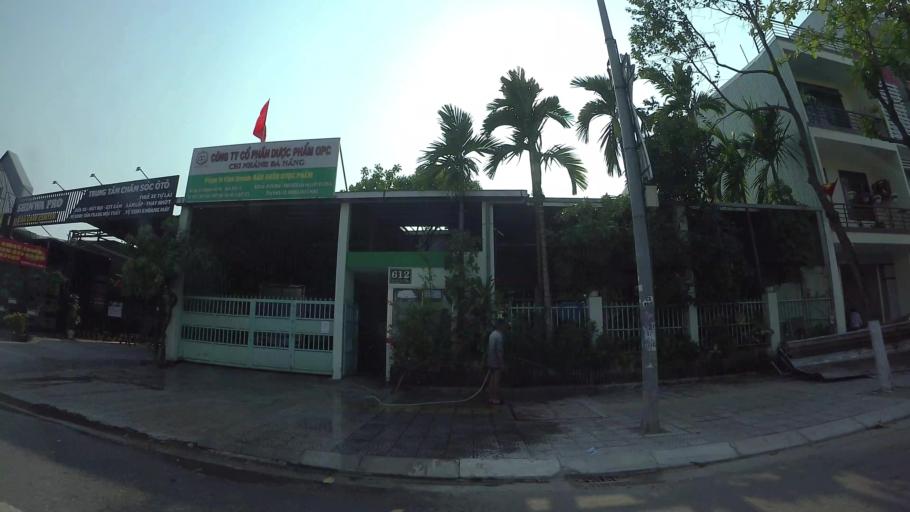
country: VN
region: Da Nang
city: Cam Le
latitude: 16.0227
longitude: 108.2097
